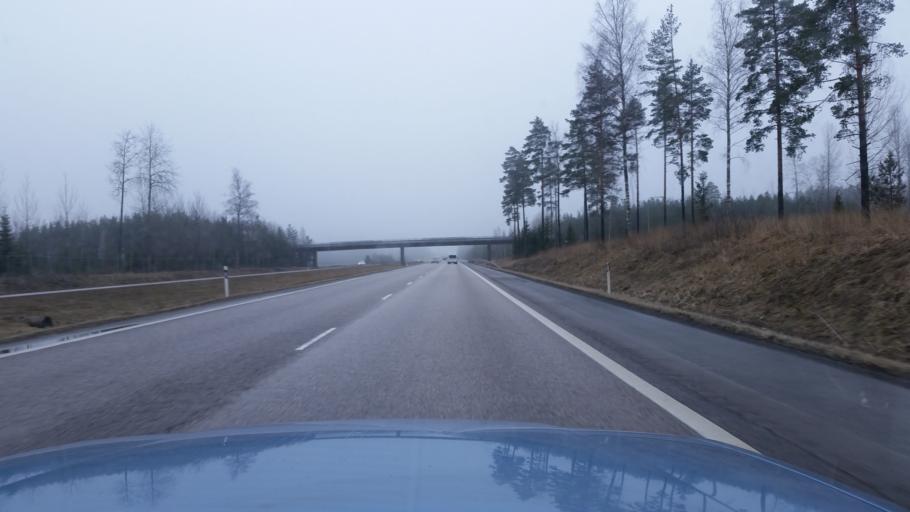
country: FI
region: Uusimaa
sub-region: Helsinki
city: Nurmijaervi
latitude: 60.5184
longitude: 24.8456
